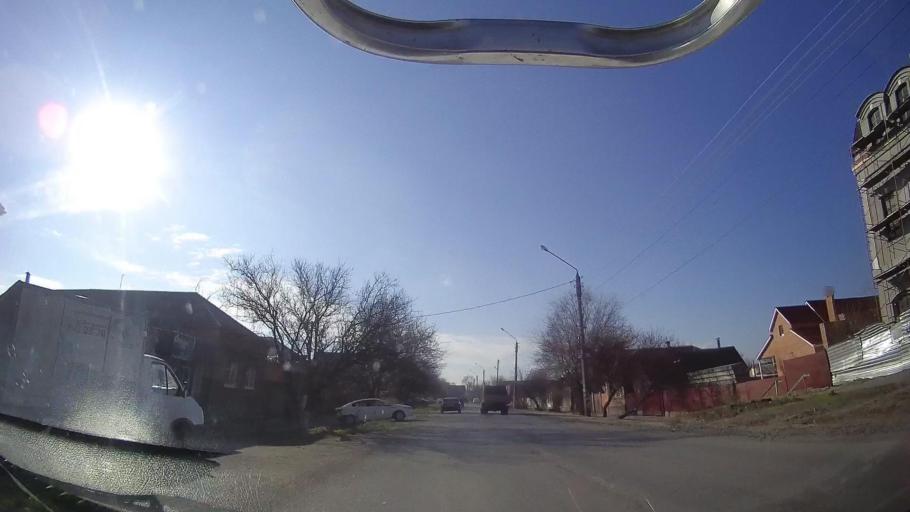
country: RU
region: Rostov
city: Bataysk
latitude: 47.1263
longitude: 39.6924
